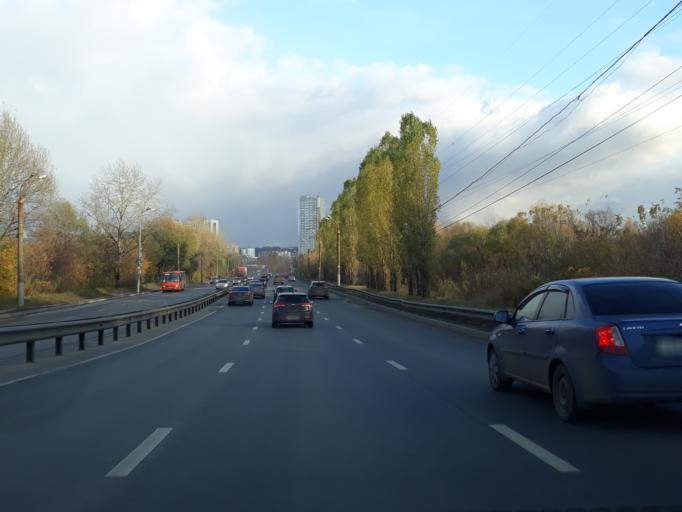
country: RU
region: Nizjnij Novgorod
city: Nizhniy Novgorod
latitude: 56.3044
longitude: 43.9100
